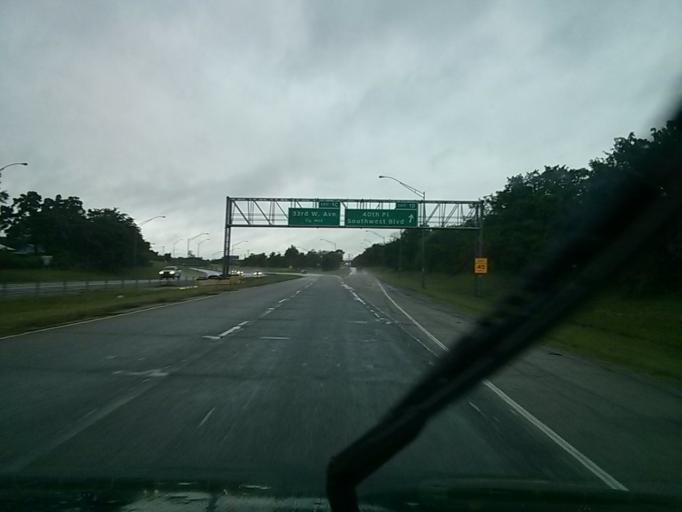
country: US
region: Oklahoma
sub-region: Tulsa County
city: Tulsa
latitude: 36.1092
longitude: -96.0170
